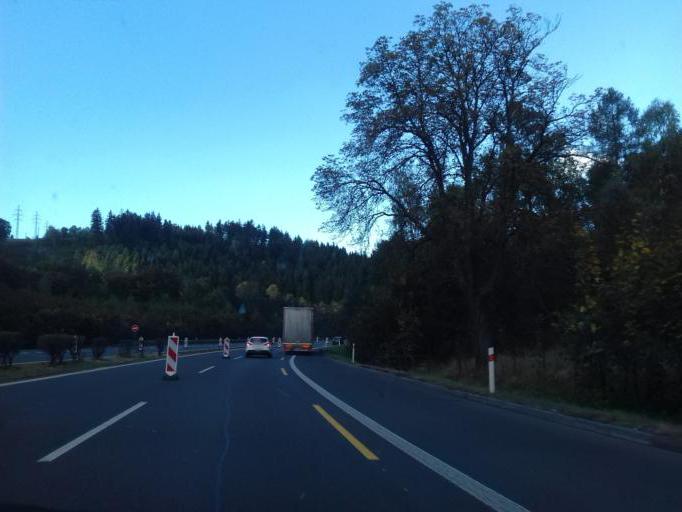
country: CZ
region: Liberecky
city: Hodkovice nad Mohelkou
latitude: 50.6810
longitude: 15.1012
